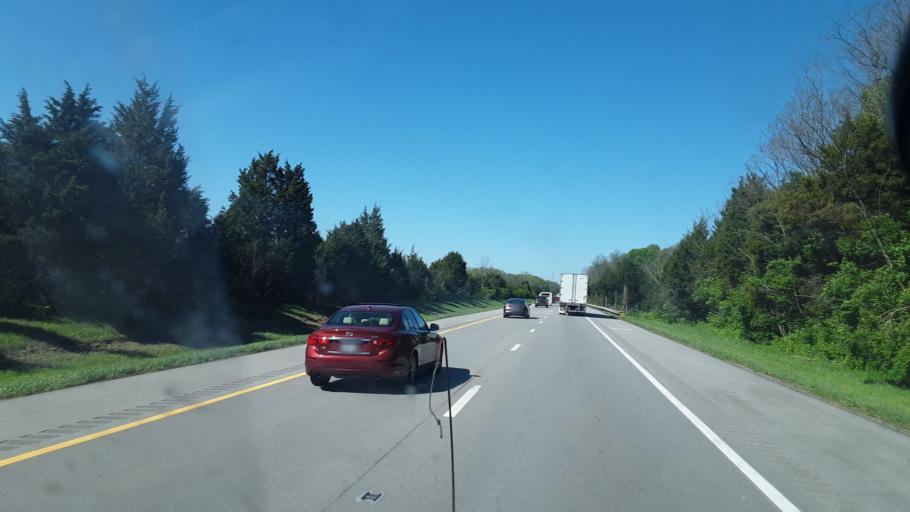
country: US
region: Ohio
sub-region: Warren County
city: South Lebanon
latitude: 39.3930
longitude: -84.1953
